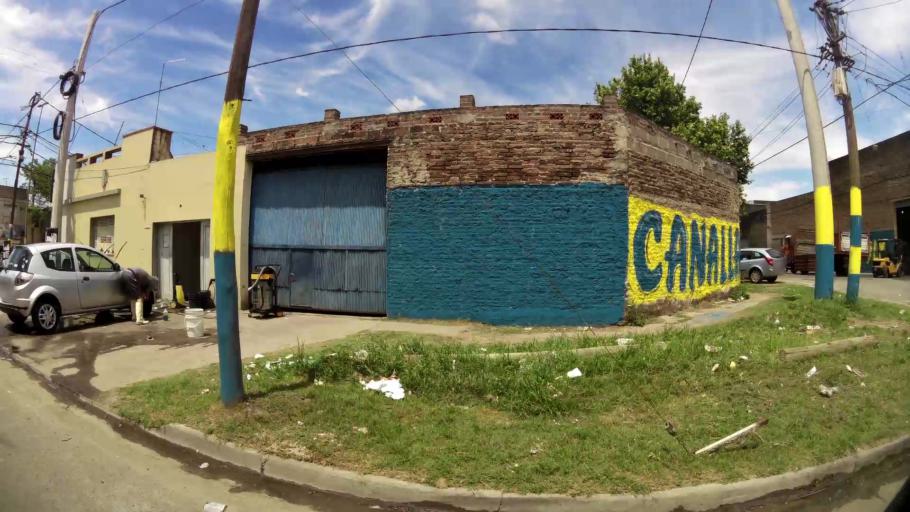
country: AR
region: Santa Fe
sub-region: Departamento de Rosario
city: Rosario
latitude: -32.9835
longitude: -60.6285
